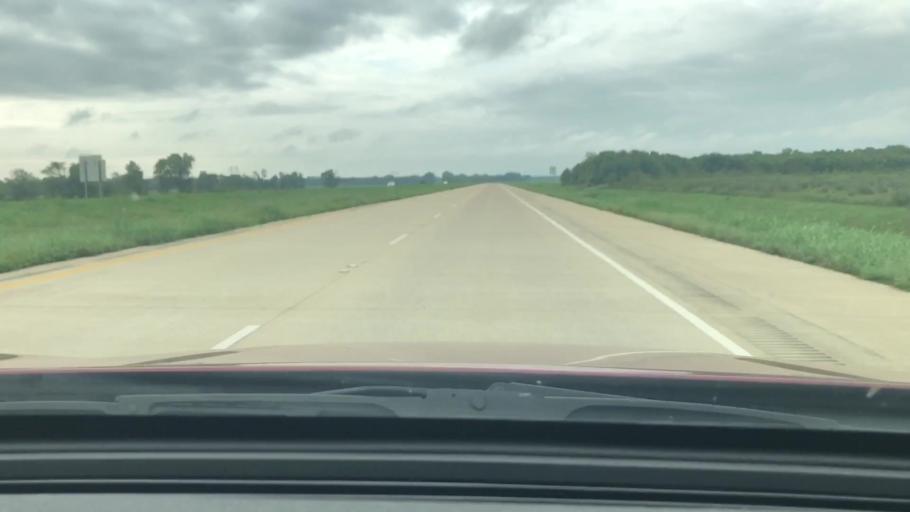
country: US
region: Louisiana
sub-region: Caddo Parish
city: Blanchard
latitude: 32.6646
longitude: -93.8461
